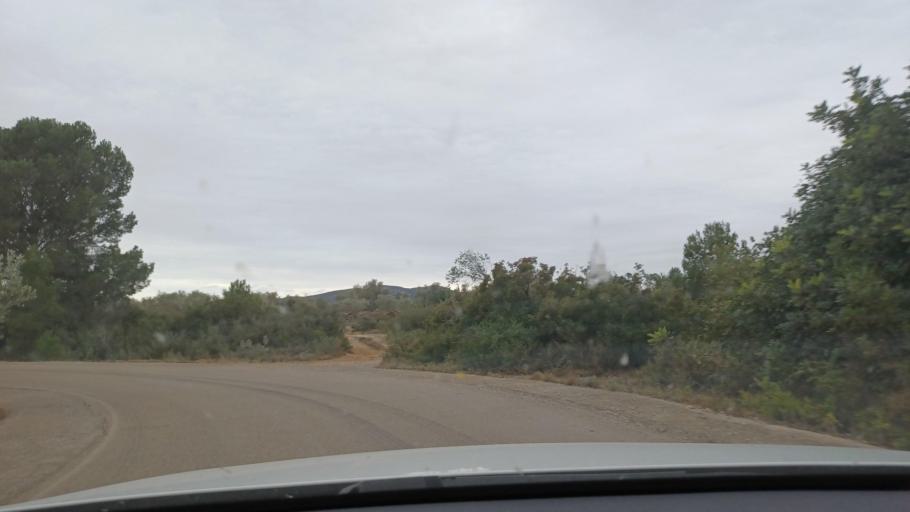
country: ES
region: Valencia
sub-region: Provincia de Castello
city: Canet lo Roig
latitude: 40.5900
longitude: 0.2810
